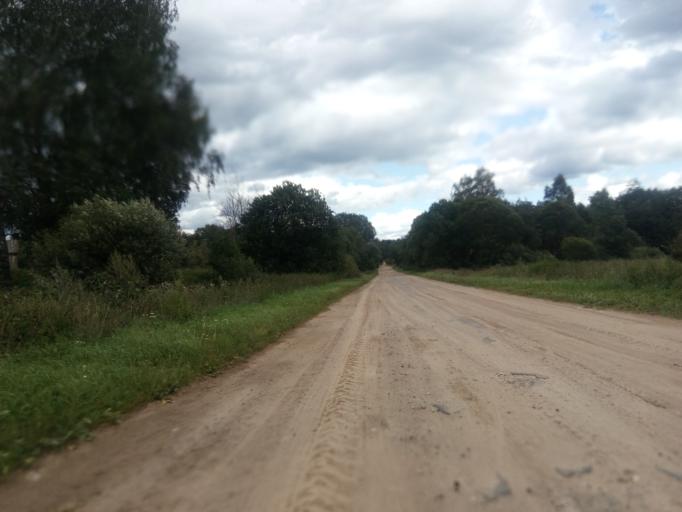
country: BY
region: Vitebsk
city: Dzisna
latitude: 55.7069
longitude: 28.3227
